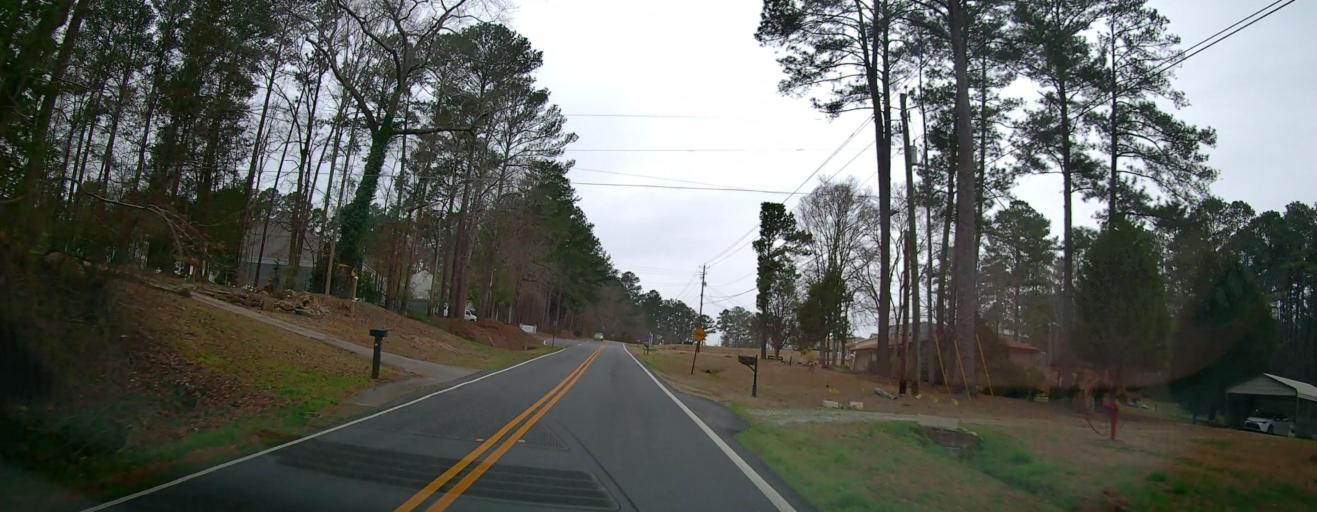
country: US
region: Georgia
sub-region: Bibb County
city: Macon
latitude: 32.9085
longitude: -83.7103
